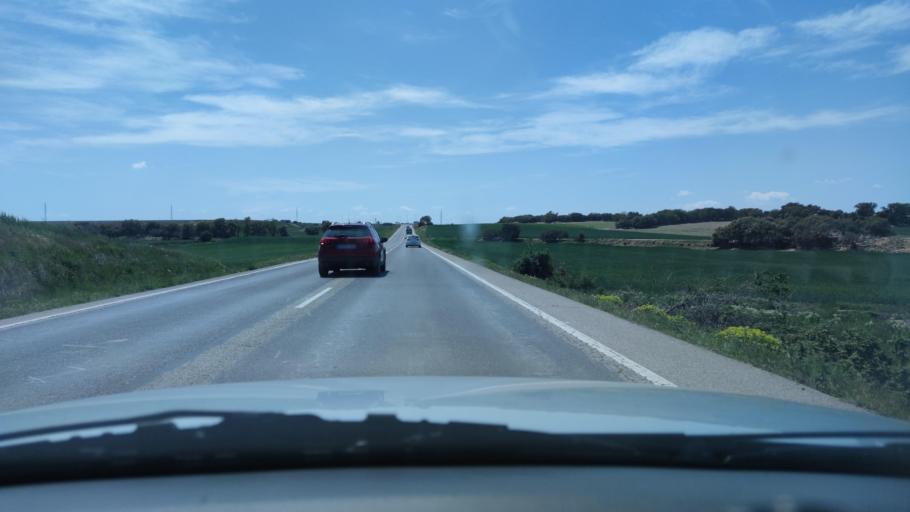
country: ES
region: Catalonia
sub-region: Provincia de Lleida
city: Mont-roig del Camp
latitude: 41.7304
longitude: 1.2100
